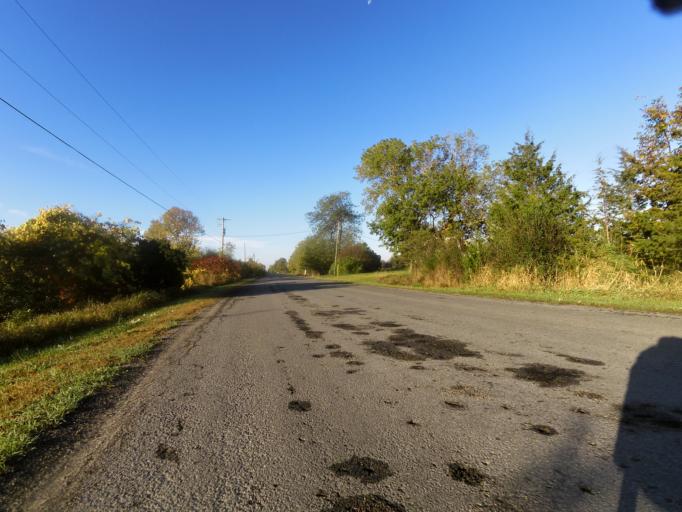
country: CA
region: Ontario
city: Belleville
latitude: 44.0314
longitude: -77.4671
